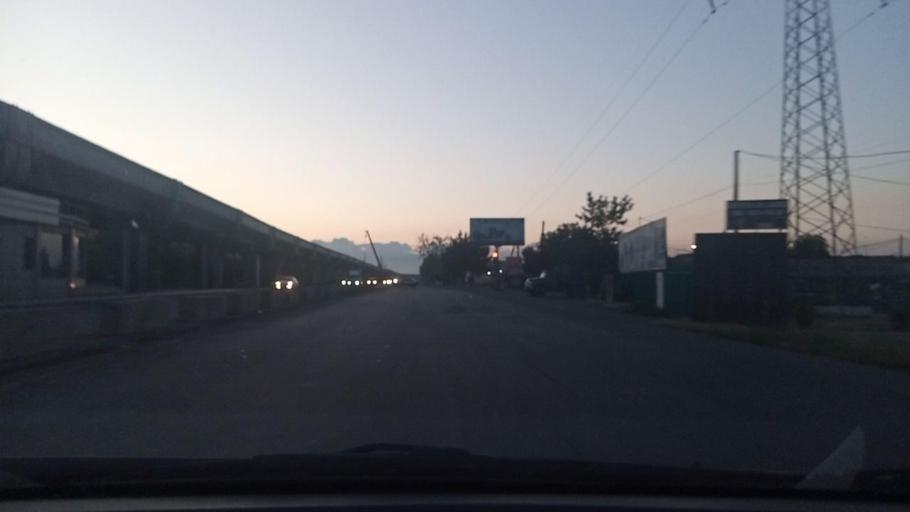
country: UZ
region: Toshkent Shahri
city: Bektemir
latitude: 41.2442
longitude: 69.3002
